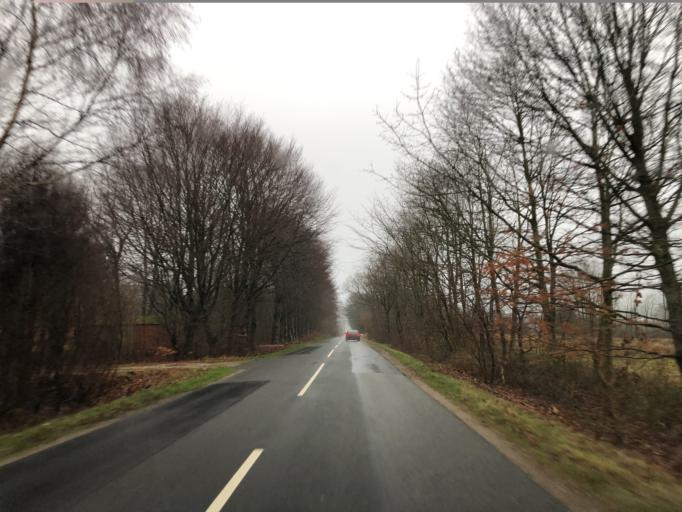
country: DK
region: Central Jutland
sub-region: Holstebro Kommune
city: Ulfborg
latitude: 56.2060
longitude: 8.4052
